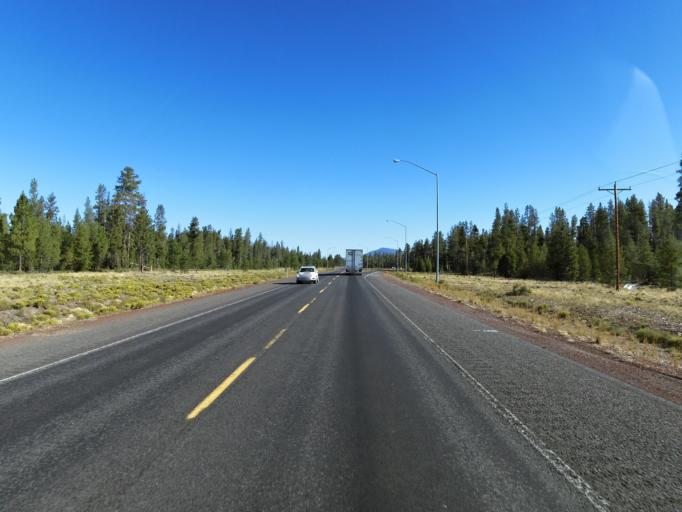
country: US
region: Oregon
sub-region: Deschutes County
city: La Pine
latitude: 43.1683
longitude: -121.7888
